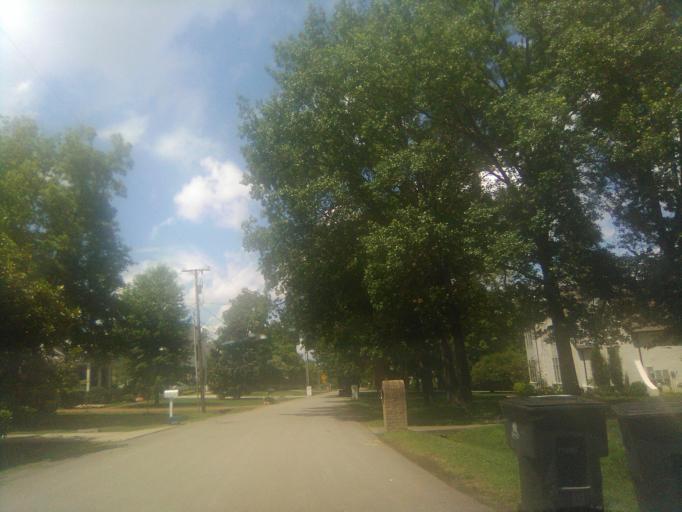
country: US
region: Tennessee
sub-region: Davidson County
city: Belle Meade
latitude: 36.1070
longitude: -86.8412
